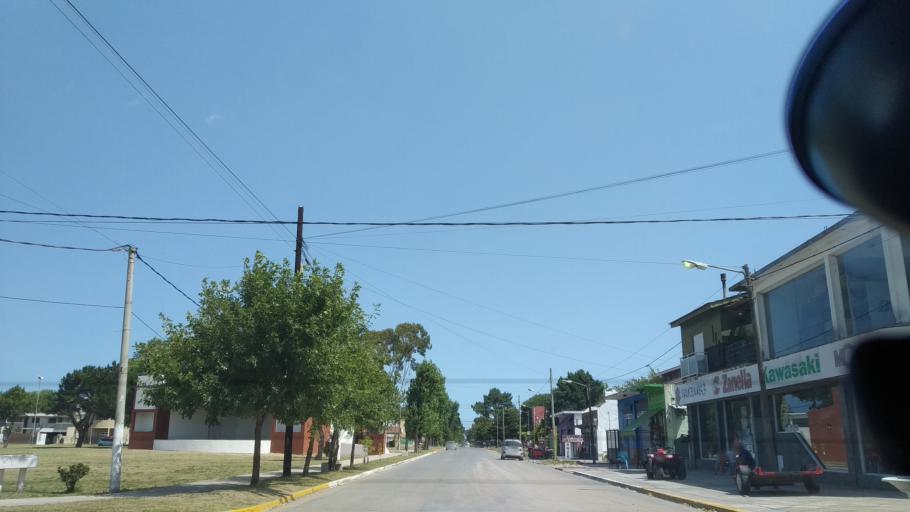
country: AR
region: Buenos Aires
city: Mar del Tuyu
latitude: -36.5699
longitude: -56.6941
